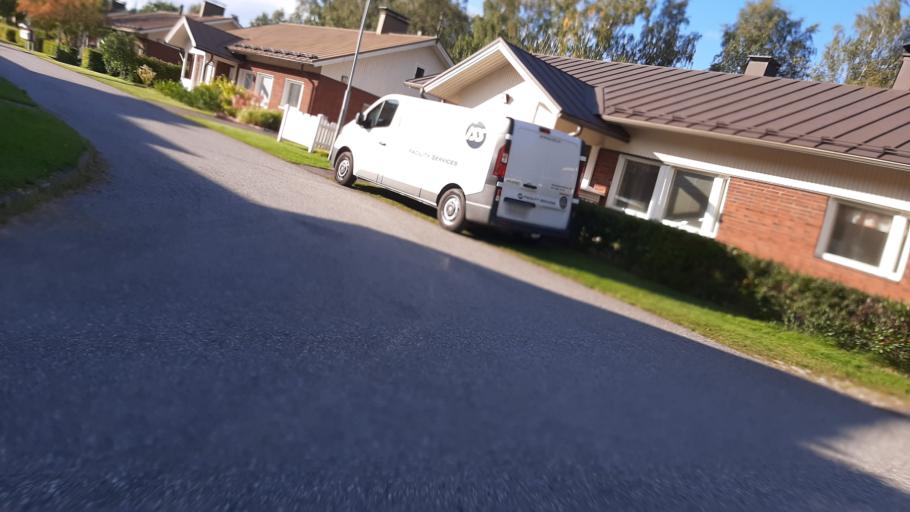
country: FI
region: North Karelia
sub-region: Joensuu
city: Joensuu
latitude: 62.6243
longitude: 29.7992
